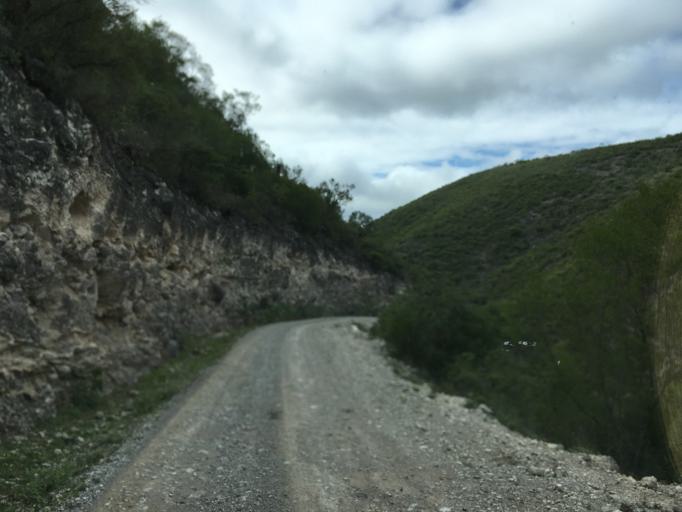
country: MX
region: Hidalgo
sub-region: Metztitlan
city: Fontezuelas
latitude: 20.6233
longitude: -98.8770
